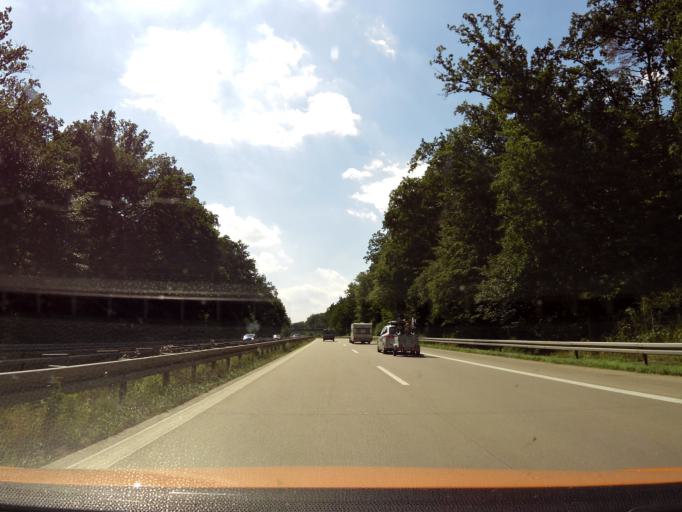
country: DE
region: Brandenburg
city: Gerswalde
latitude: 53.1142
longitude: 13.8633
